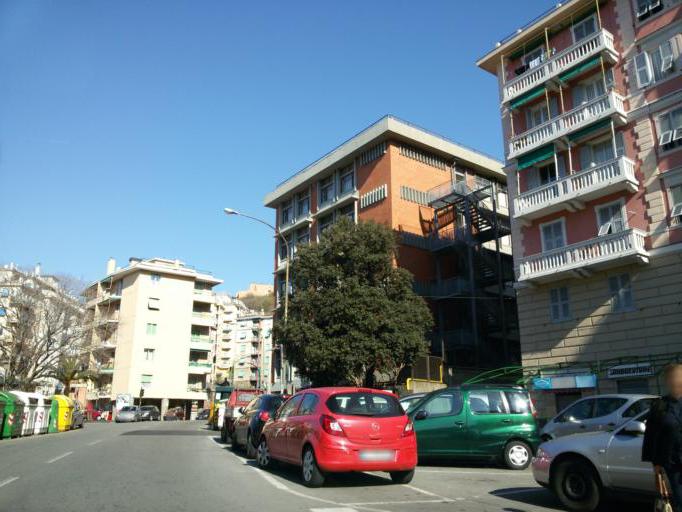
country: IT
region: Liguria
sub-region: Provincia di Genova
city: San Teodoro
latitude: 44.4193
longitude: 8.9146
